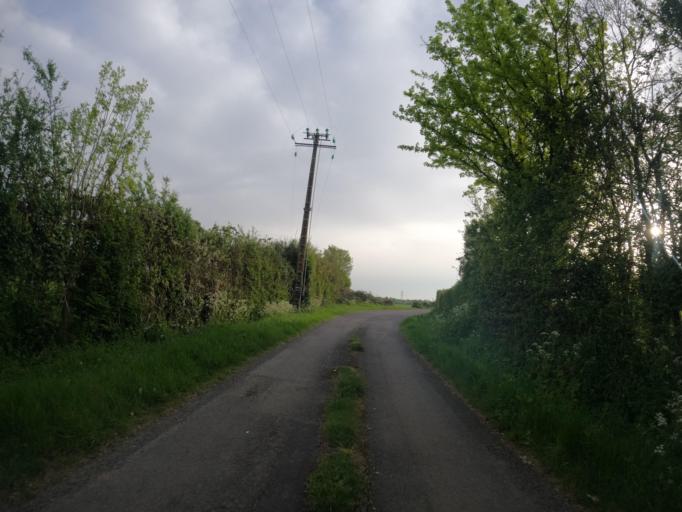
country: FR
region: Poitou-Charentes
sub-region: Departement des Deux-Sevres
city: Moncoutant
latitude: 46.7293
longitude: -0.5622
